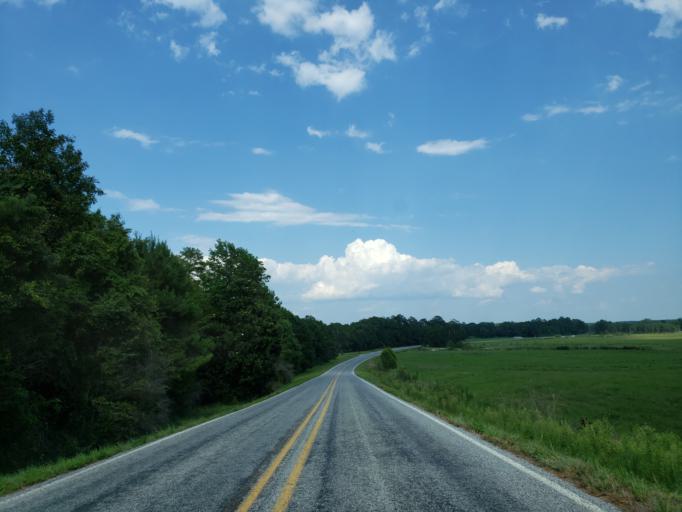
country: US
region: Mississippi
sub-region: Jones County
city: Ellisville
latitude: 31.6236
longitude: -89.3645
